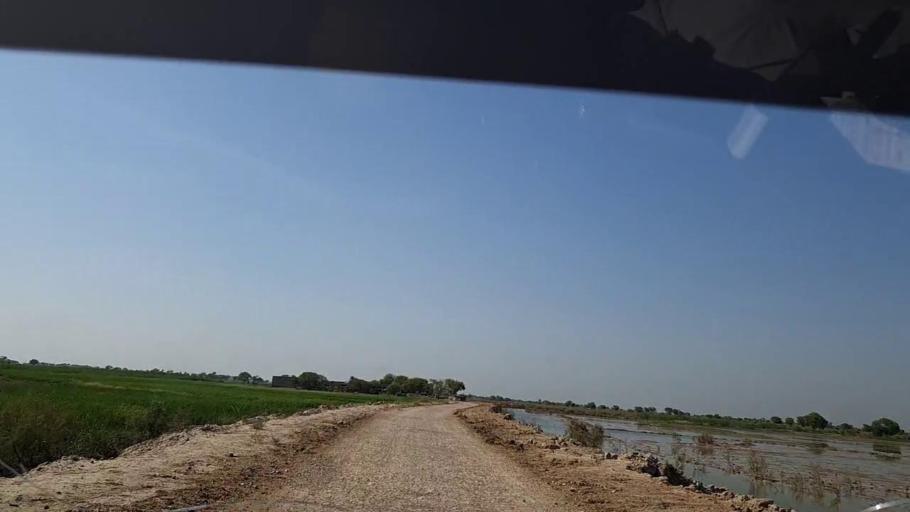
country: PK
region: Sindh
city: Tangwani
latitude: 28.3257
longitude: 69.0808
